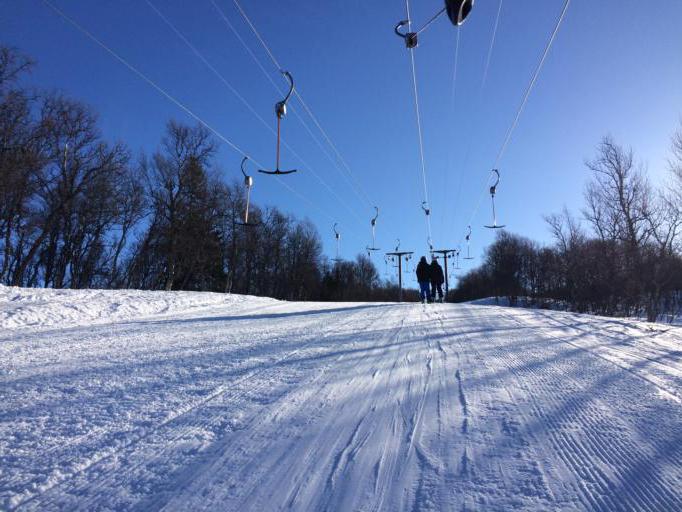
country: SE
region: Jaemtland
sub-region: Are Kommun
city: Are
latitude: 63.4303
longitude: 13.0198
